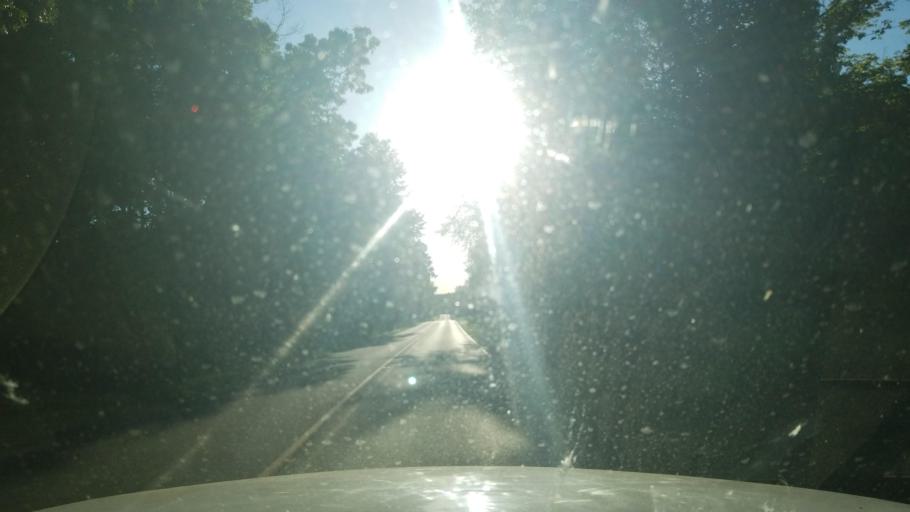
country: US
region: Illinois
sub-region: Hardin County
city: Elizabethtown
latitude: 37.5777
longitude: -88.3773
